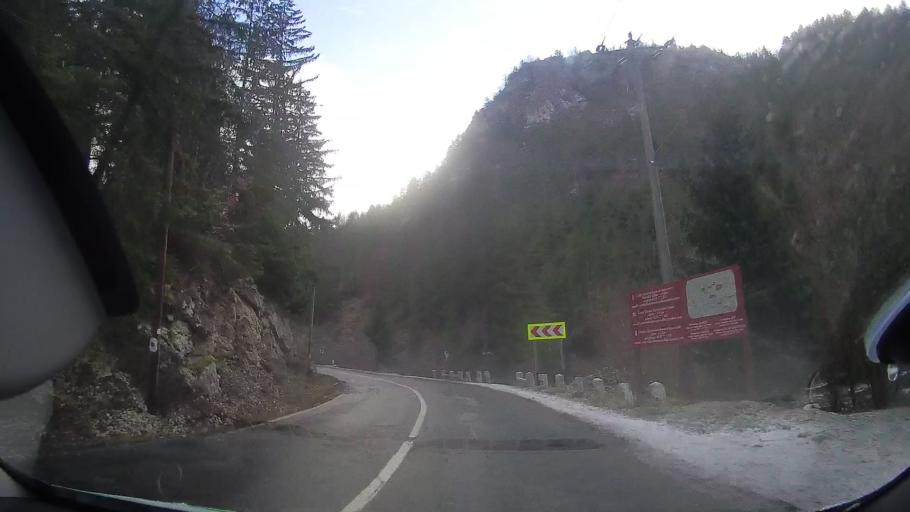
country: RO
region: Alba
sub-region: Comuna Albac
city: Albac
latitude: 46.4561
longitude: 22.9375
